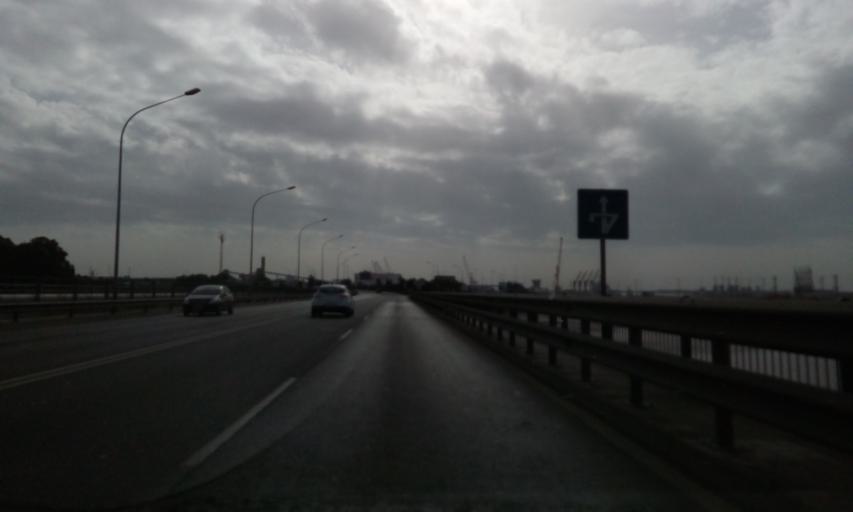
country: ES
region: Andalusia
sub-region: Provincia de Huelva
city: Punta Umbria
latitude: 37.2068
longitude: -6.9372
